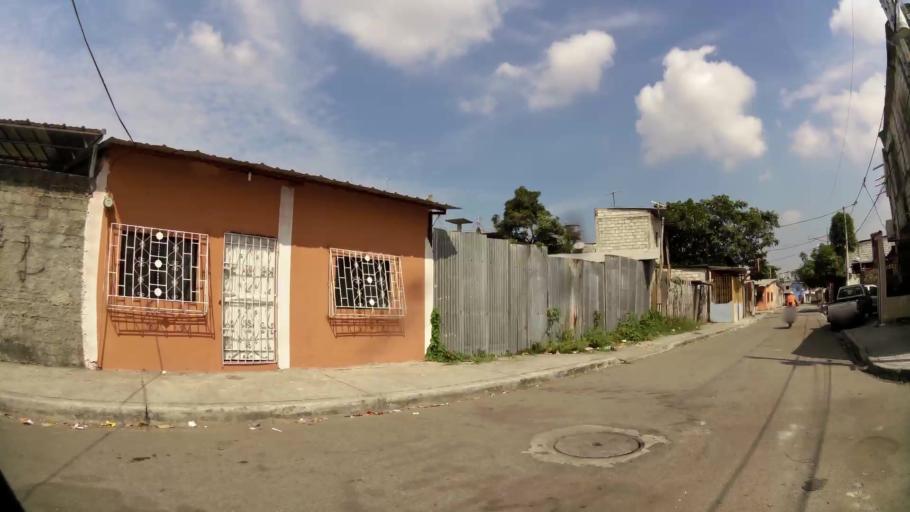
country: EC
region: Guayas
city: Guayaquil
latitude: -2.2632
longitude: -79.8842
